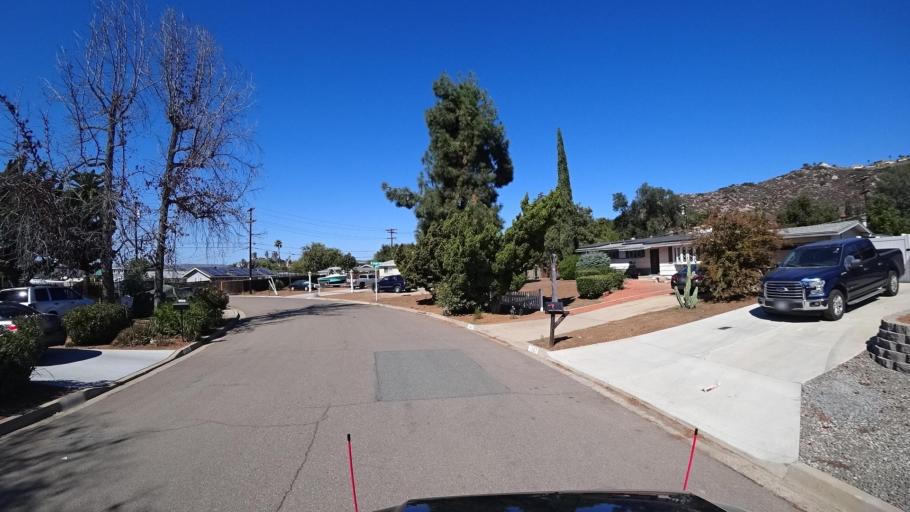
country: US
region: California
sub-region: San Diego County
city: Santee
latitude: 32.8271
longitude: -116.9588
